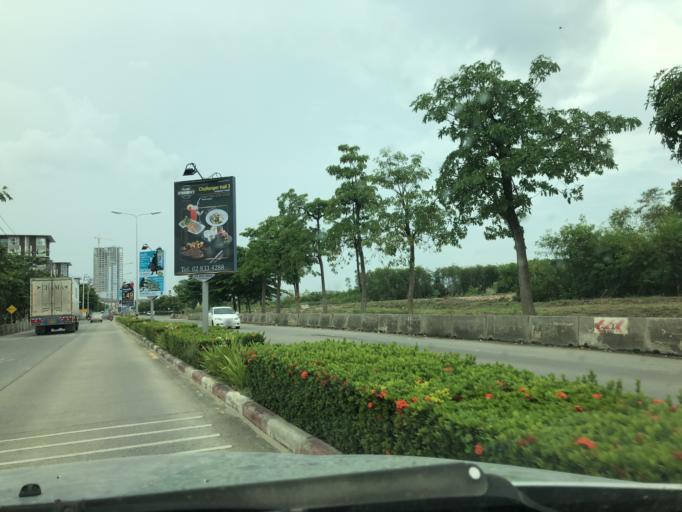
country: TH
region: Bangkok
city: Don Mueang
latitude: 13.9237
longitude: 100.5447
